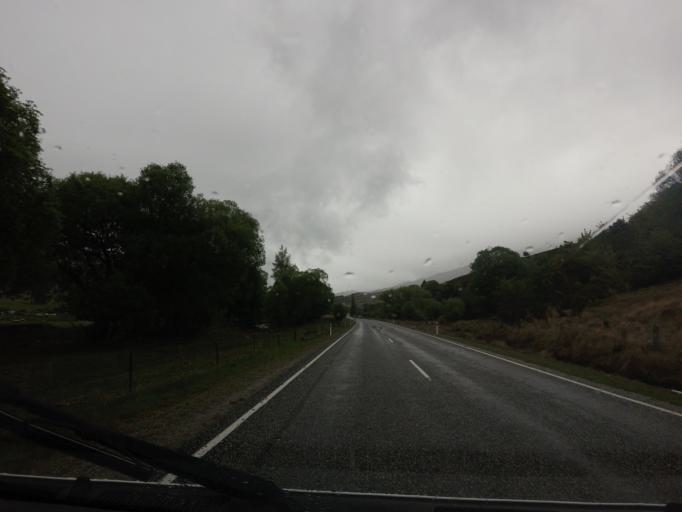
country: NZ
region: Otago
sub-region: Queenstown-Lakes District
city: Arrowtown
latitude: -44.8715
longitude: 169.0140
